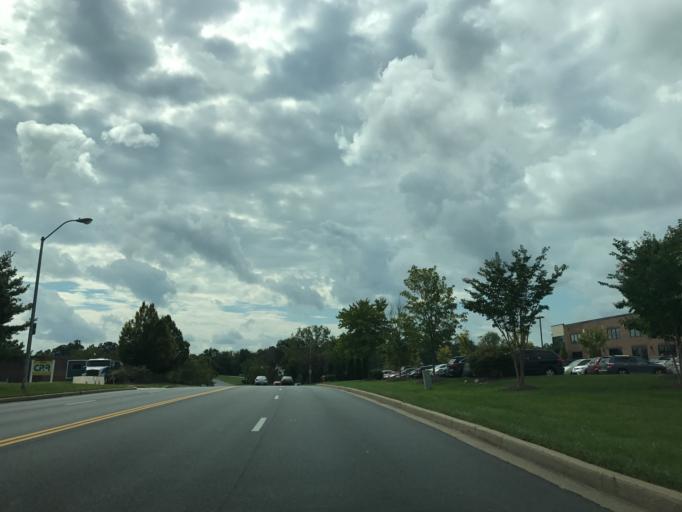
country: US
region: Maryland
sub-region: Baltimore County
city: Milford Mill
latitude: 39.3330
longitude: -76.7528
